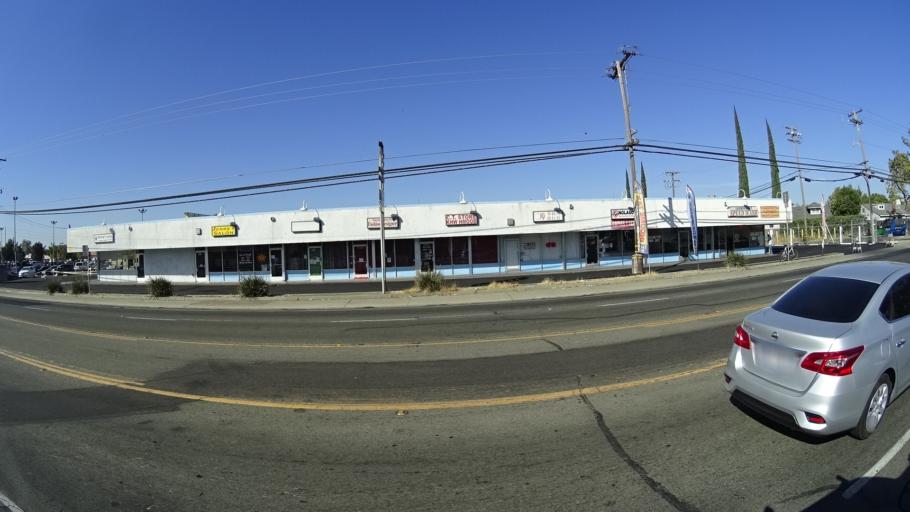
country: US
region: California
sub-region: Sacramento County
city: Parkway
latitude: 38.4976
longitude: -121.4827
